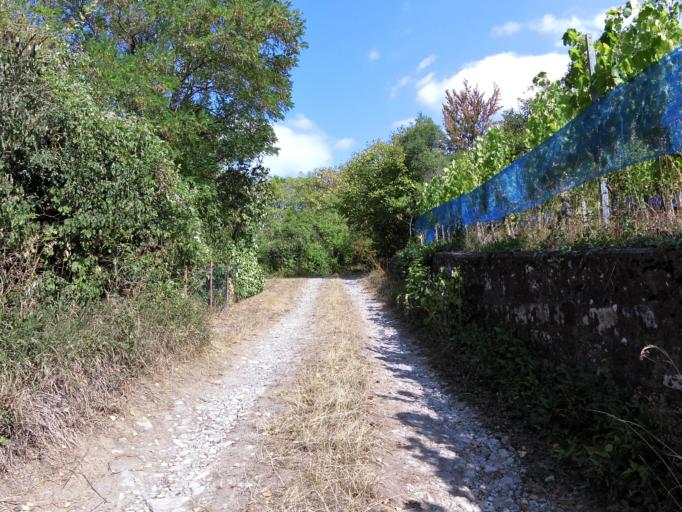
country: DE
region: Bavaria
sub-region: Regierungsbezirk Unterfranken
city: Gerbrunn
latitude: 49.7568
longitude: 10.0058
